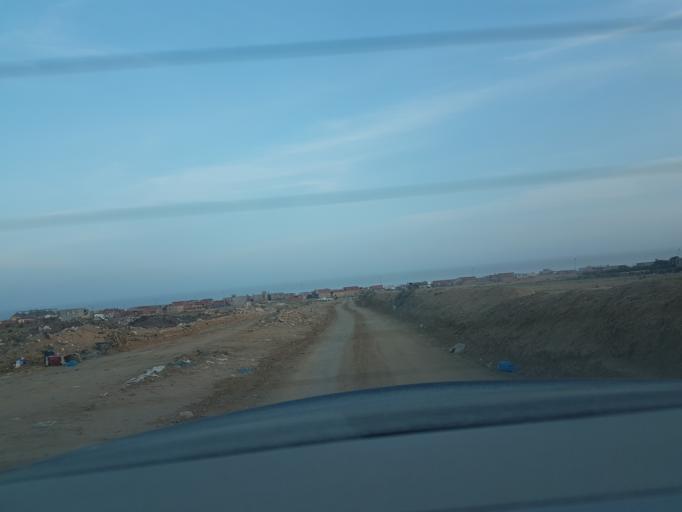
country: TN
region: Safaqis
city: Sfax
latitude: 34.7034
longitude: 10.6968
